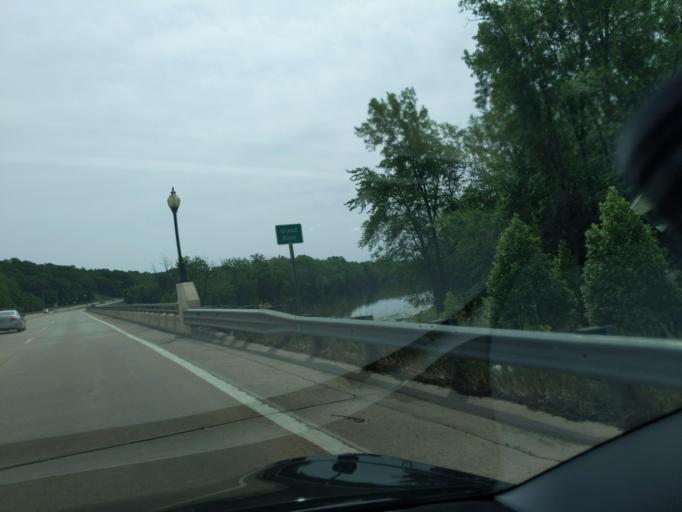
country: US
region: Michigan
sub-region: Kent County
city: Forest Hills
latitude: 42.9553
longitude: -85.4766
